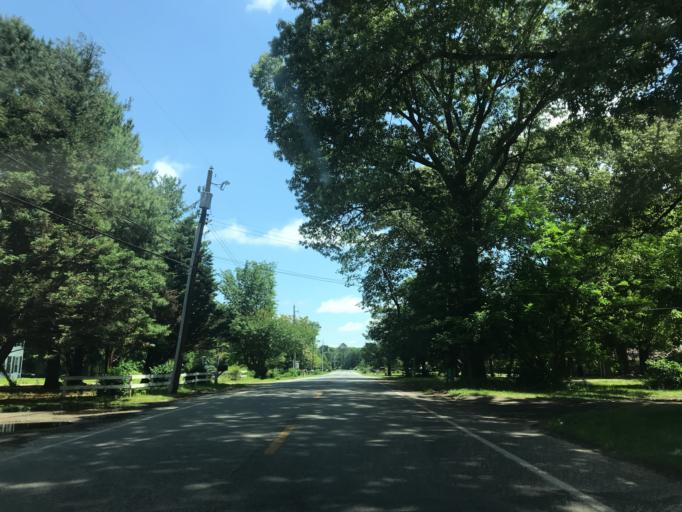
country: US
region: Maryland
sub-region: Caroline County
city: Federalsburg
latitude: 38.6948
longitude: -75.7506
